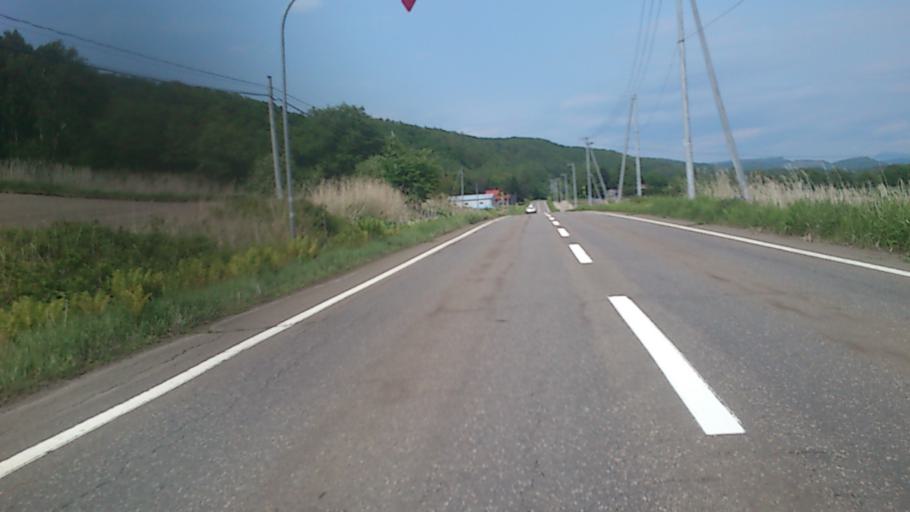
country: JP
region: Hokkaido
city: Otofuke
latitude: 43.2581
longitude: 143.5720
